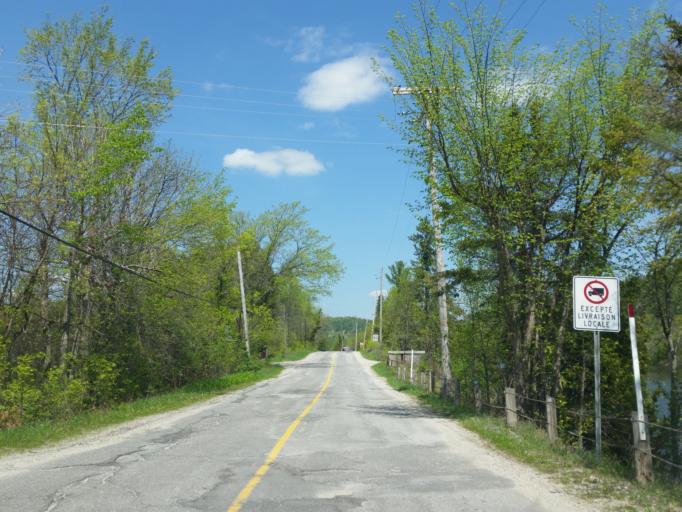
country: CA
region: Quebec
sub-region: Outaouais
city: Wakefield
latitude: 45.6166
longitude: -75.8990
